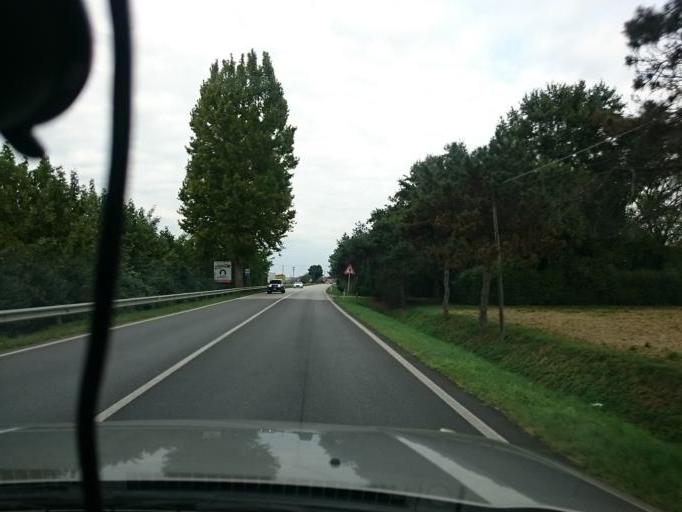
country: IT
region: Veneto
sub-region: Provincia di Padova
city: Arlesega
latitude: 45.4674
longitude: 11.7120
